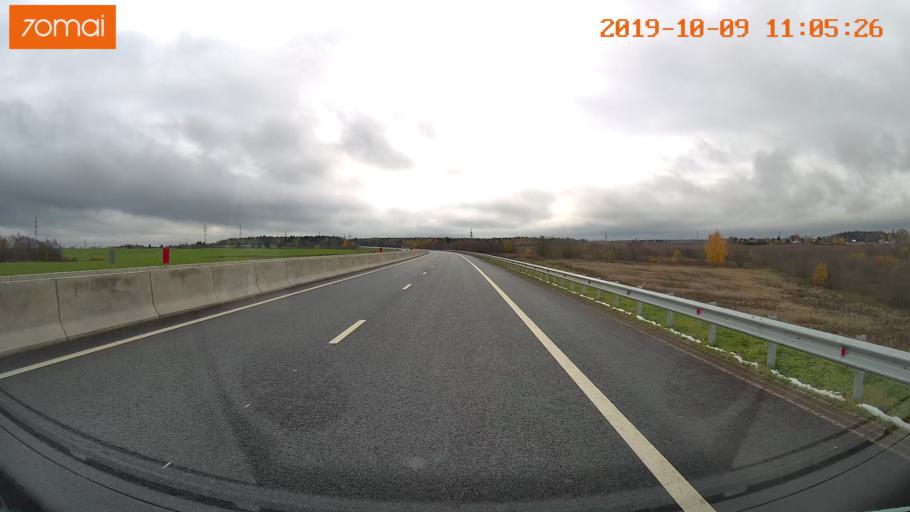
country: RU
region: Vologda
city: Molochnoye
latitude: 59.2001
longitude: 39.7591
